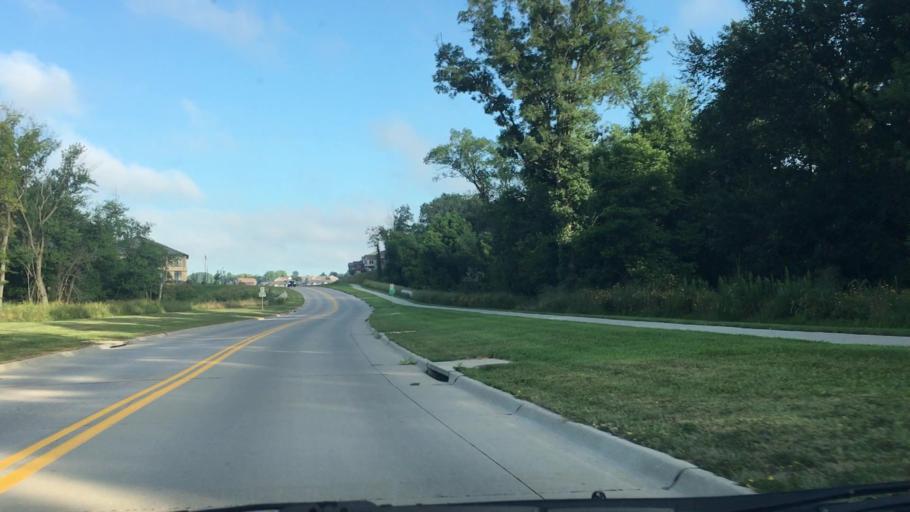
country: US
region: Iowa
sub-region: Johnson County
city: Coralville
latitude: 41.7001
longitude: -91.5503
